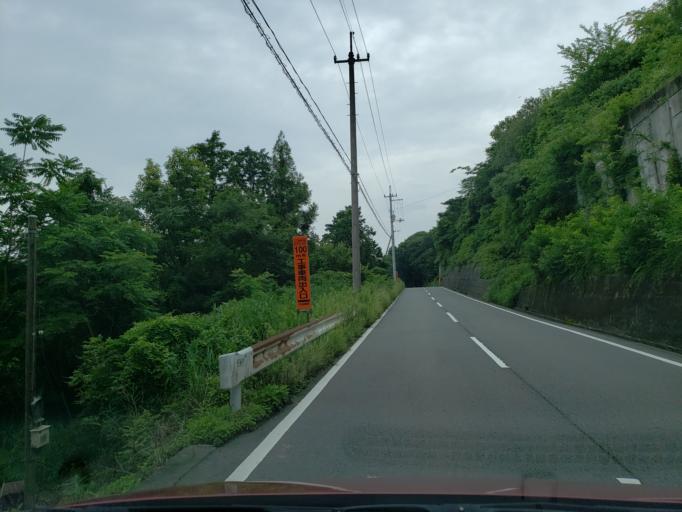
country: JP
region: Tokushima
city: Wakimachi
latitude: 34.1051
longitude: 134.2465
